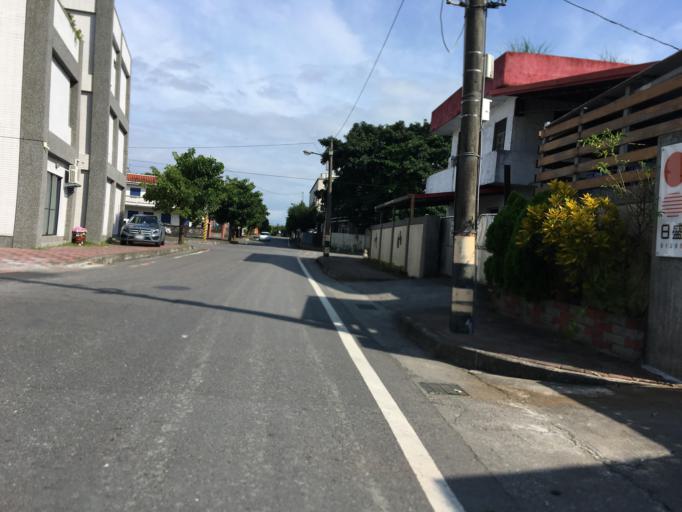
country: TW
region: Taiwan
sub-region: Yilan
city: Yilan
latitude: 24.6347
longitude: 121.8283
